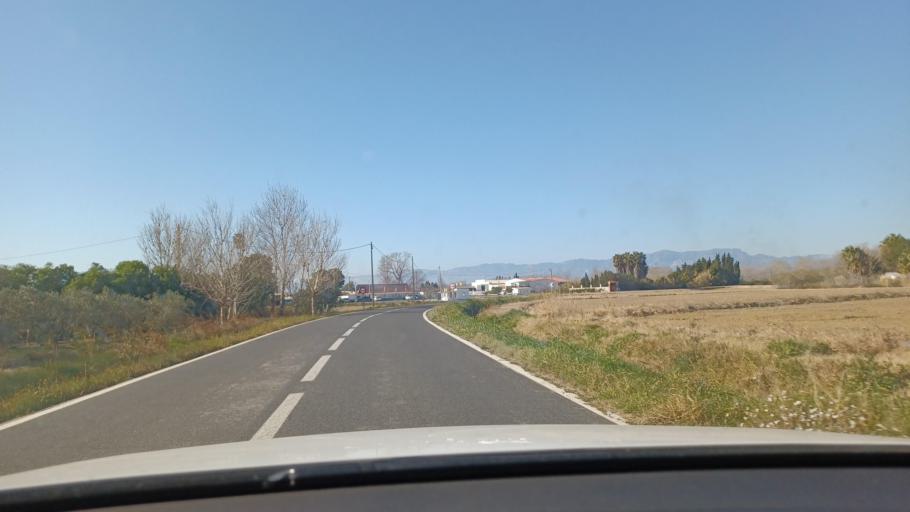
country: ES
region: Catalonia
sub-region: Provincia de Tarragona
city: Amposta
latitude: 40.7046
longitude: 0.6272
